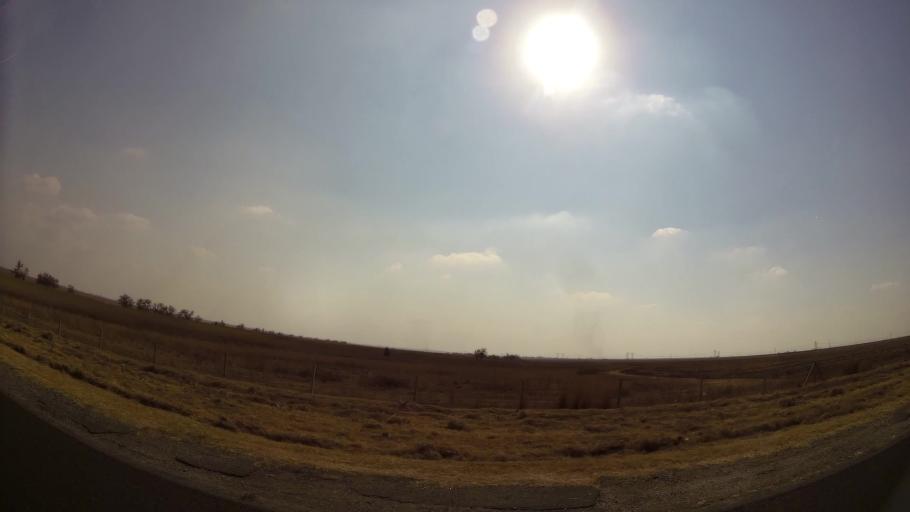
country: ZA
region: Gauteng
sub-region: Ekurhuleni Metropolitan Municipality
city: Springs
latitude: -26.1650
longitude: 28.4631
